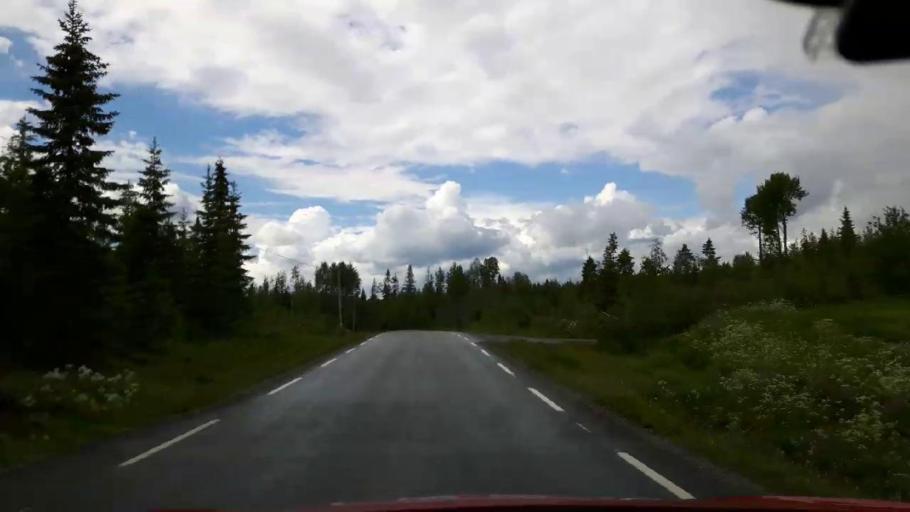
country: NO
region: Nord-Trondelag
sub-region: Lierne
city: Sandvika
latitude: 64.0983
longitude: 14.0328
